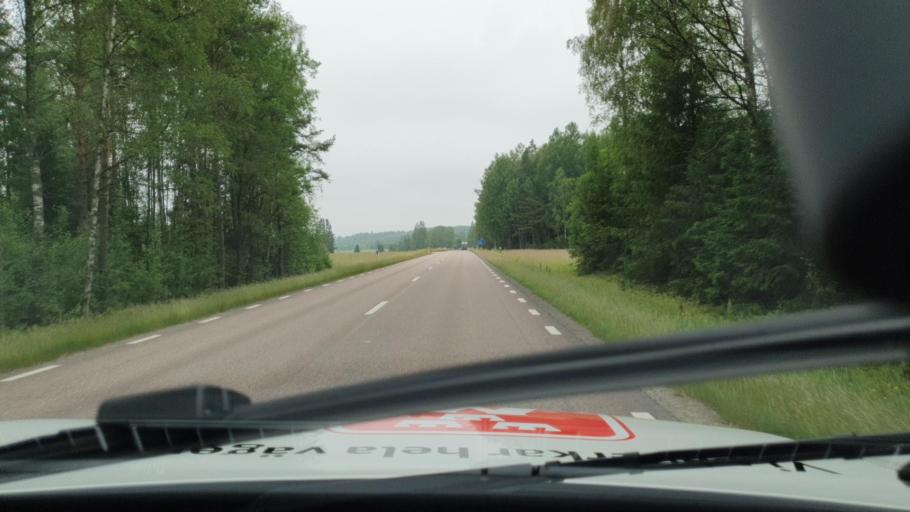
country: SE
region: Vaermland
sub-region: Sunne Kommun
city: Sunne
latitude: 59.6826
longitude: 13.1400
